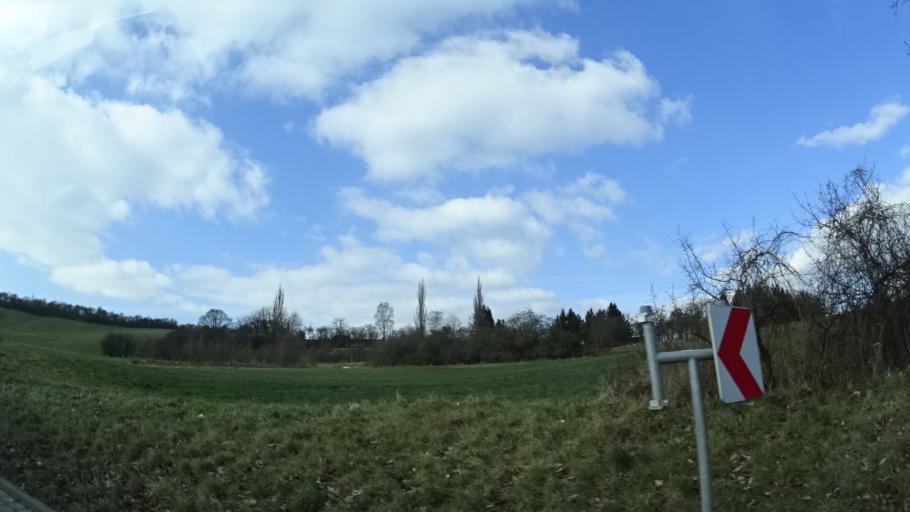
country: DE
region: Thuringia
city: Rippershausen
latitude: 50.5841
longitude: 10.3400
